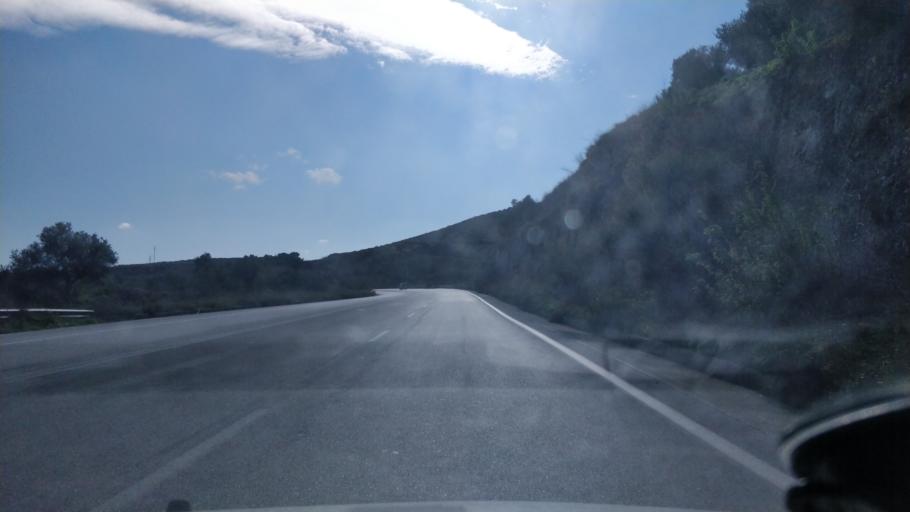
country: GR
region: Crete
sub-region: Nomos Irakleiou
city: Ano Arhanes
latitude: 35.2512
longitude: 25.1776
